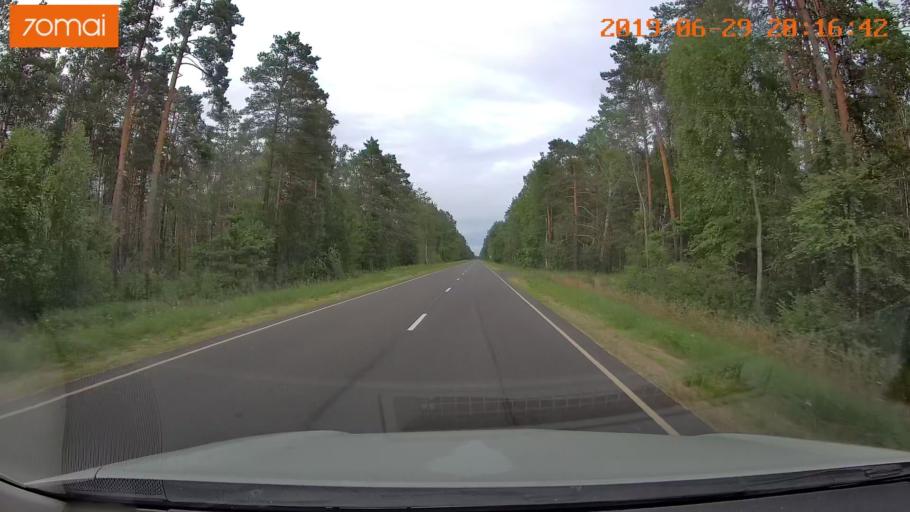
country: BY
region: Brest
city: Asnyezhytsy
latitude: 52.3830
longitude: 26.2014
